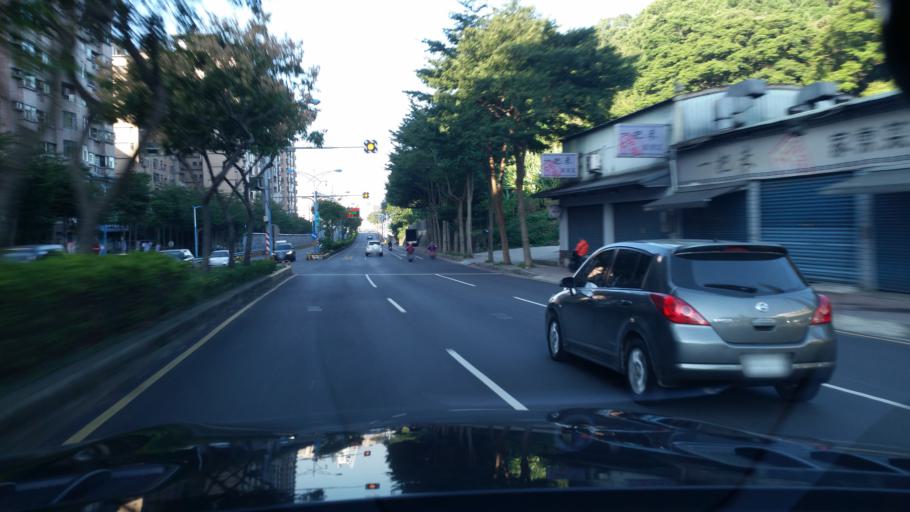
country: TW
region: Taiwan
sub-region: Taoyuan
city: Taoyuan
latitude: 24.9972
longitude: 121.3327
